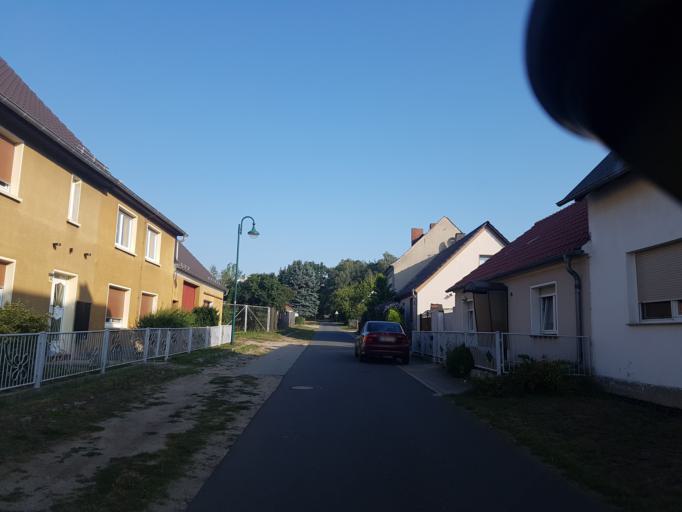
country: DE
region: Saxony-Anhalt
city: Kropstadt
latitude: 51.9689
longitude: 12.7438
